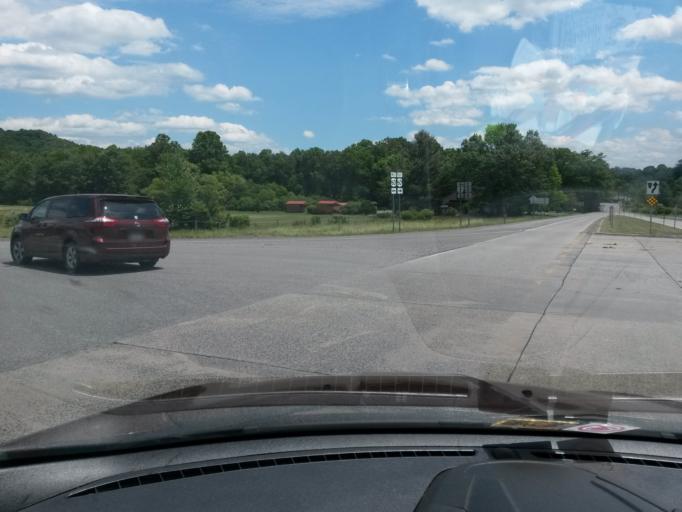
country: US
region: West Virginia
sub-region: Greenbrier County
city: Rainelle
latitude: 37.9027
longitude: -80.6328
